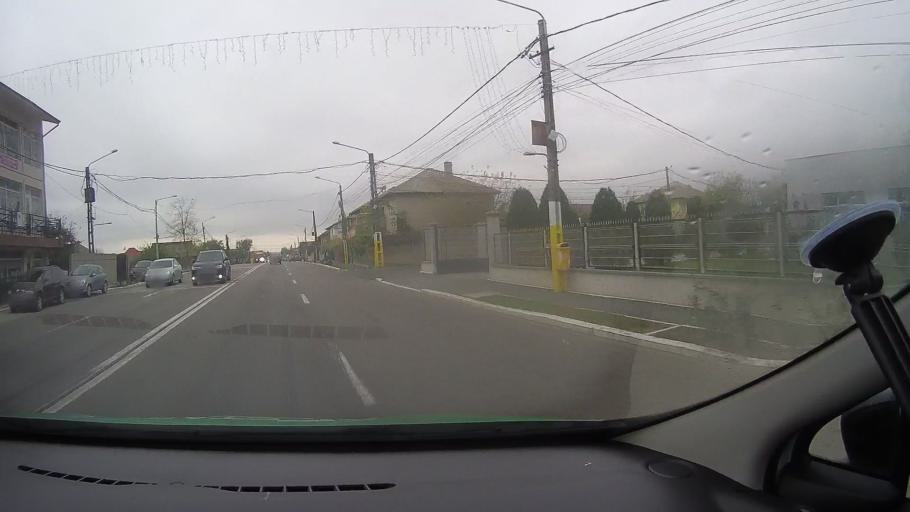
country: RO
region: Constanta
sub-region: Comuna Valu lui Traian
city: Valu lui Traian
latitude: 44.1663
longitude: 28.4618
